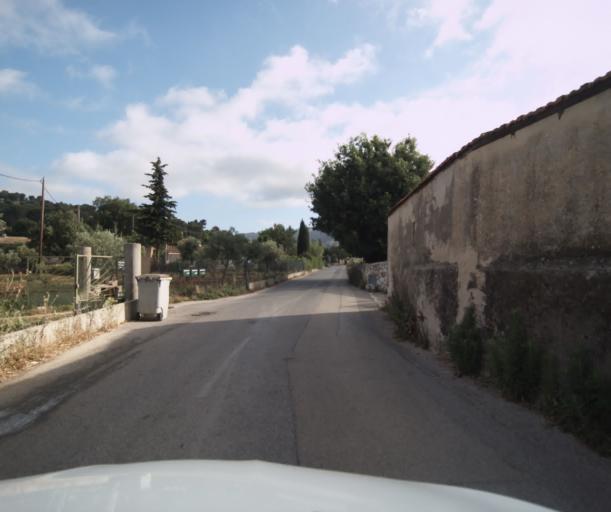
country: FR
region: Provence-Alpes-Cote d'Azur
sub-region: Departement du Var
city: Ollioules
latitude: 43.1257
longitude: 5.8433
